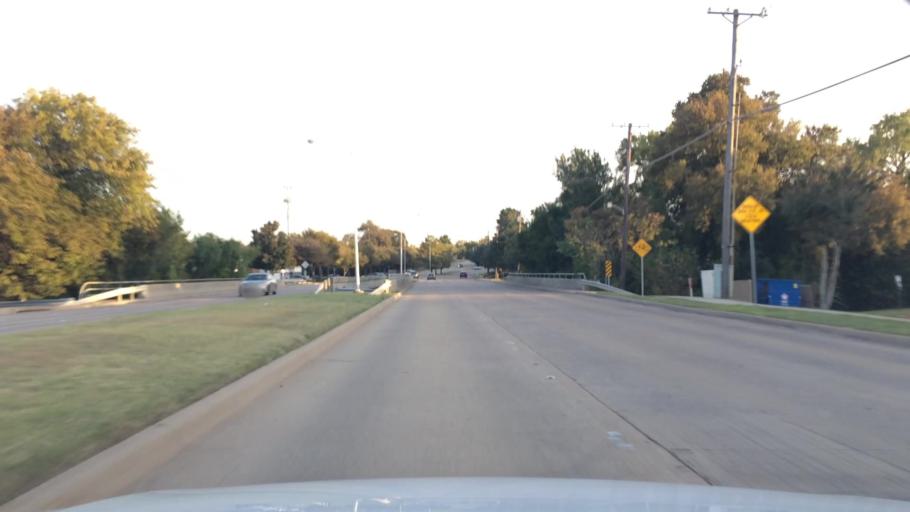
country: US
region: Texas
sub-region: Collin County
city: Allen
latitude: 33.0767
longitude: -96.7108
